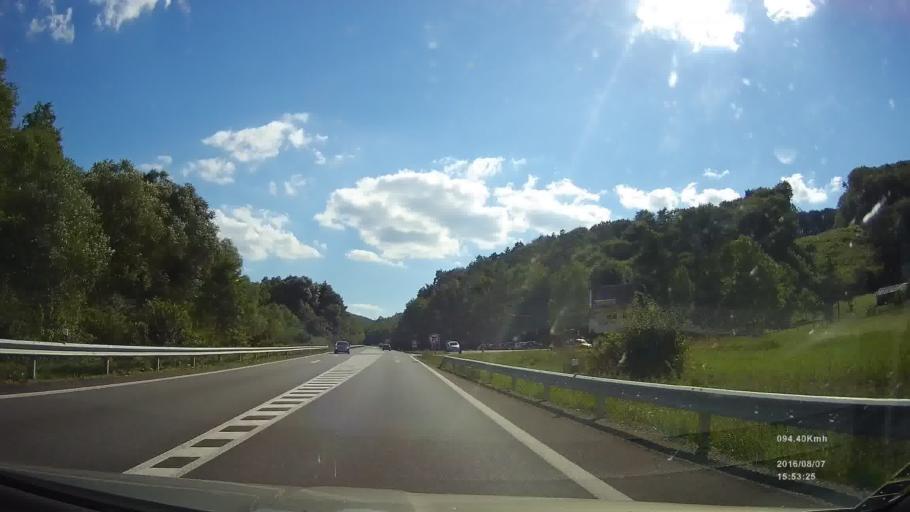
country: SK
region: Presovsky
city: Giraltovce
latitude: 49.0998
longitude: 21.4532
